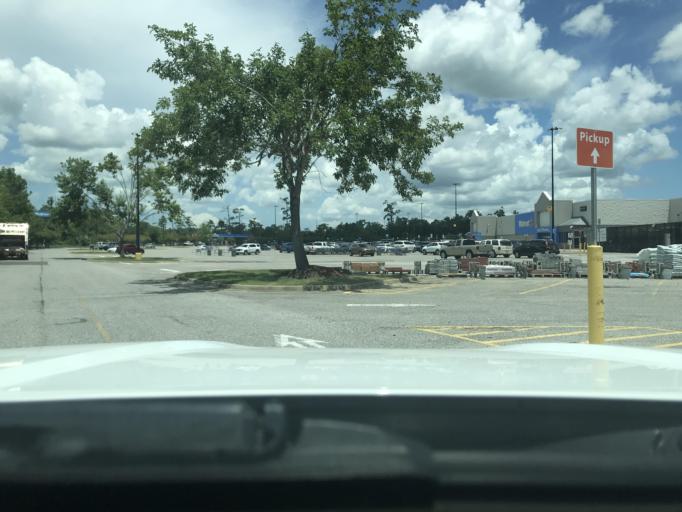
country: US
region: Louisiana
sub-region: Calcasieu Parish
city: Moss Bluff
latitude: 30.2680
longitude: -93.1810
